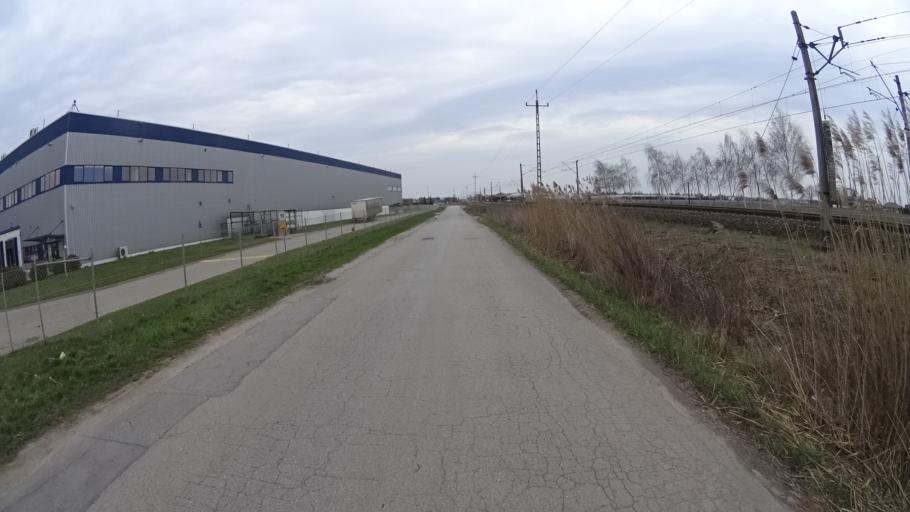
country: PL
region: Masovian Voivodeship
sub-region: Powiat warszawski zachodni
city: Ozarow Mazowiecki
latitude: 52.2083
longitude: 20.7737
